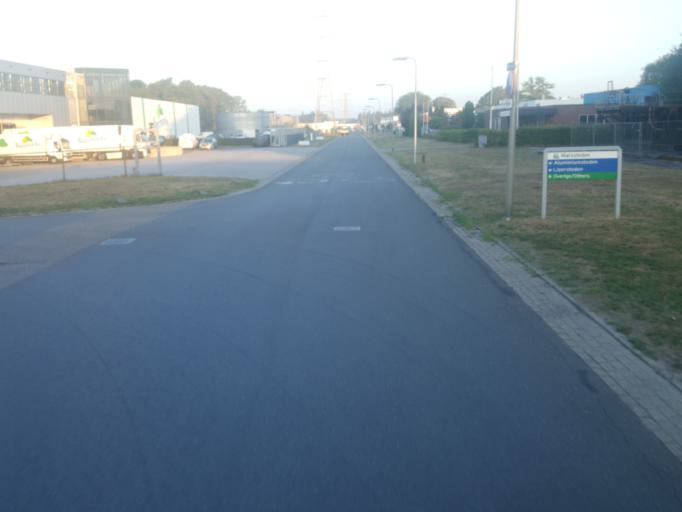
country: NL
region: Overijssel
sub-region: Gemeente Hengelo
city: Hengelo
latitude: 52.2139
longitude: 6.8243
